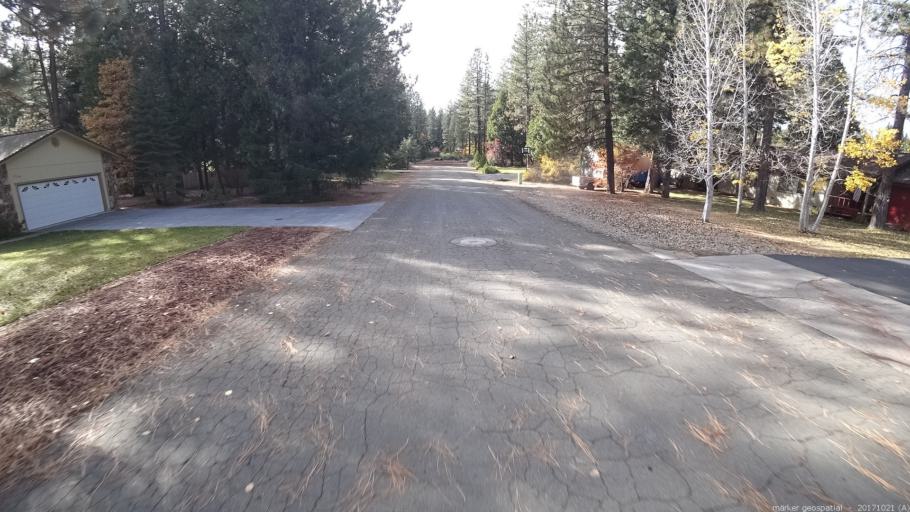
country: US
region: California
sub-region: Shasta County
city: Burney
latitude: 40.8730
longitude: -121.6657
